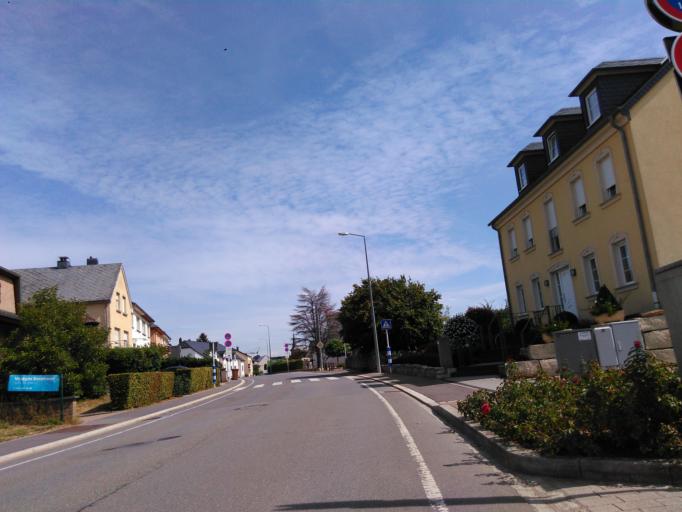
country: LU
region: Luxembourg
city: Fentange
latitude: 49.5624
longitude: 6.1503
